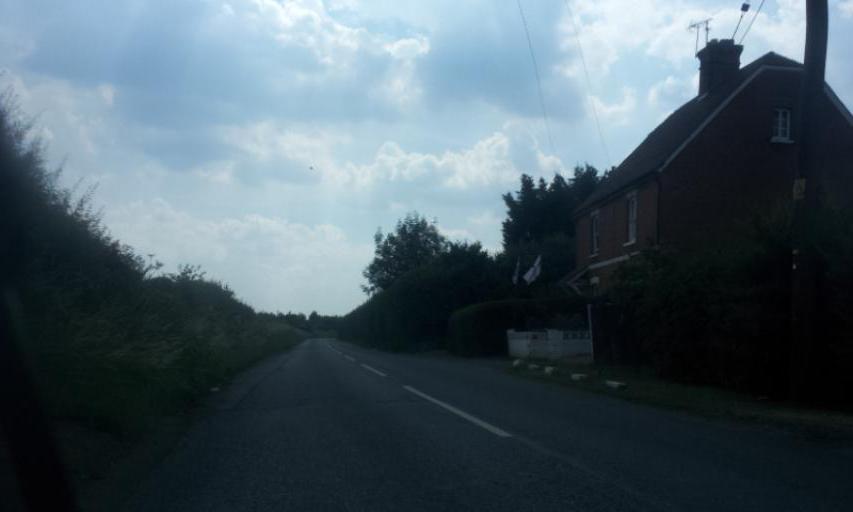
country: GB
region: England
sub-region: Kent
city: Yalding
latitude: 51.2130
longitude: 0.4181
